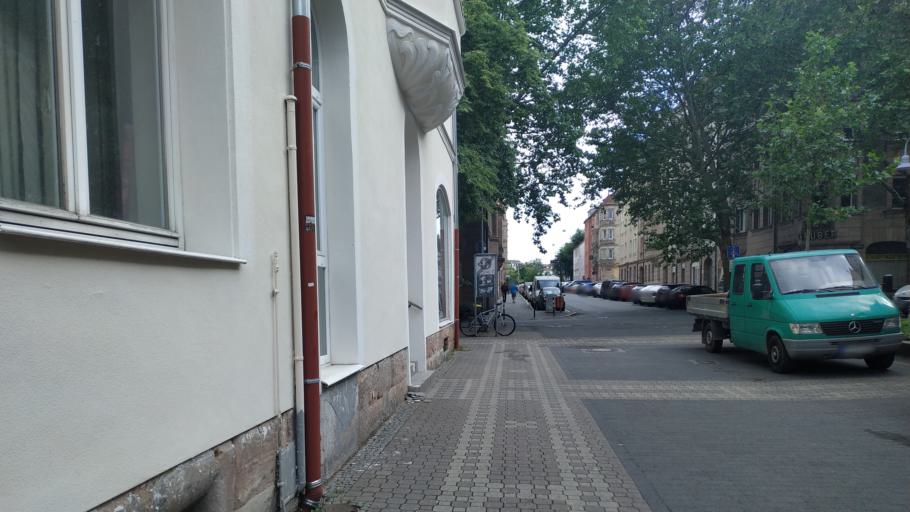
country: DE
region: Bavaria
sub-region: Regierungsbezirk Mittelfranken
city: Grossreuth bei Schweinau
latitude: 49.4379
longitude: 11.0498
